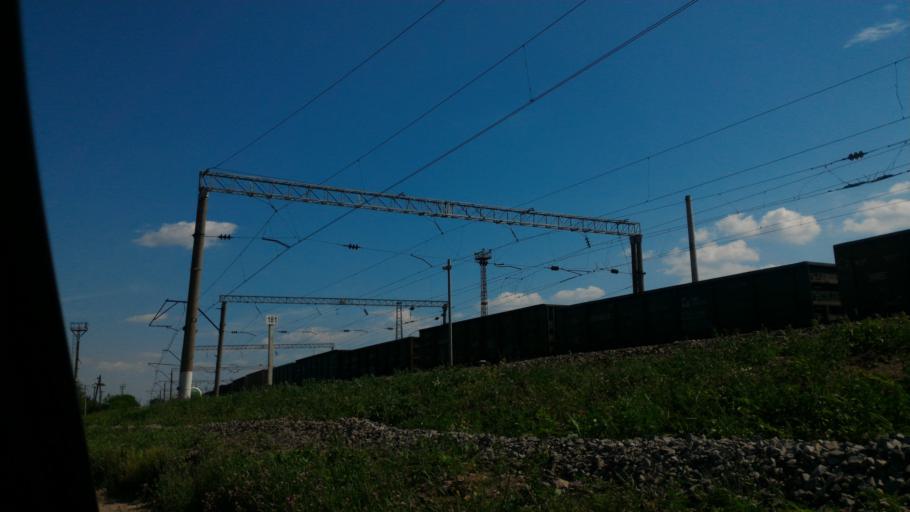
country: RU
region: Rjazan
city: Rybnoye
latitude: 54.7292
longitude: 39.5101
